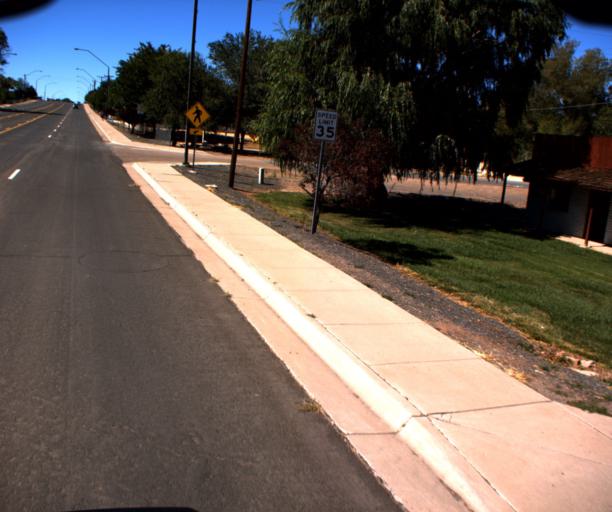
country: US
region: Arizona
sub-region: Apache County
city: Saint Johns
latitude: 34.5067
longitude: -109.3740
